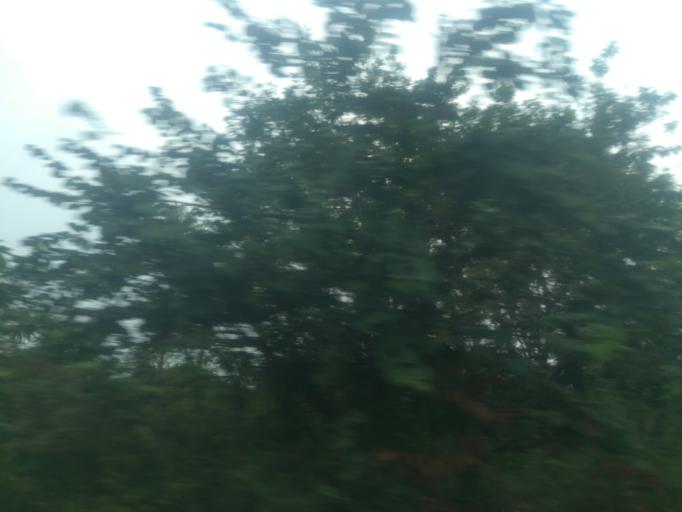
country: NG
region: Ogun
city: Ayetoro
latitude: 7.2612
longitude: 3.1110
